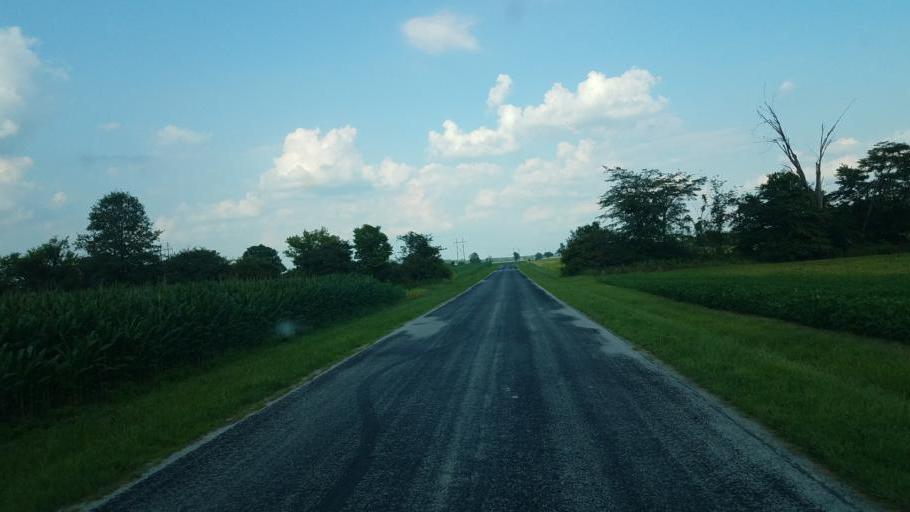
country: US
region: Ohio
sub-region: Union County
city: Richwood
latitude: 40.5609
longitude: -83.3861
